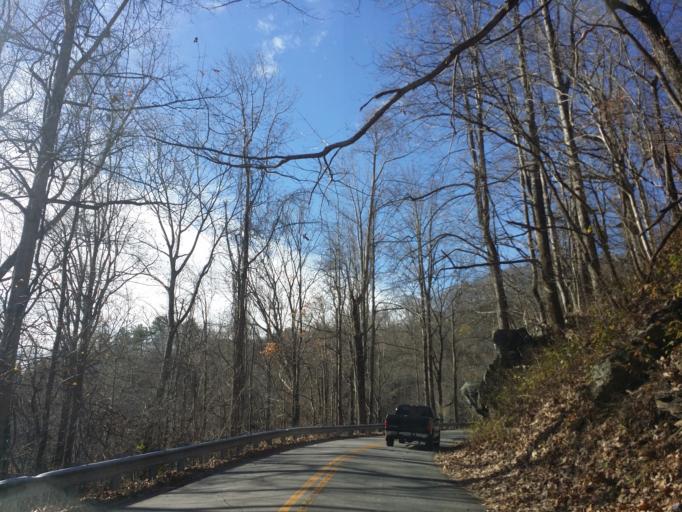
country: US
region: North Carolina
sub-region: McDowell County
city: Marion
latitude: 35.7665
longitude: -82.1613
